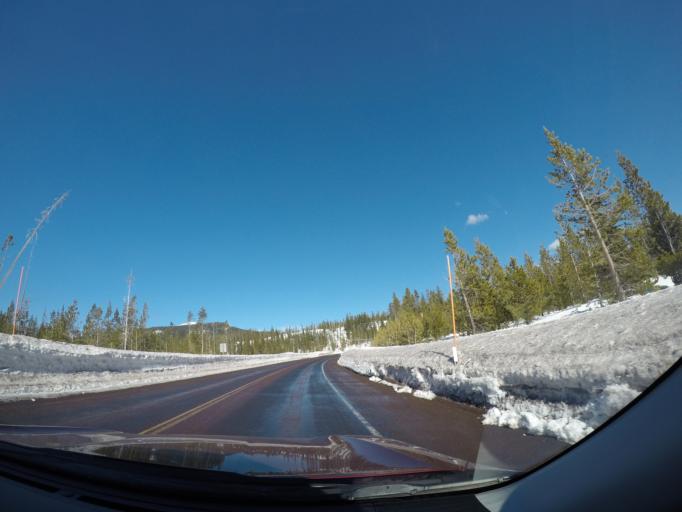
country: US
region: Oregon
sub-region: Deschutes County
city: Sunriver
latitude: 43.9805
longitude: -121.6131
